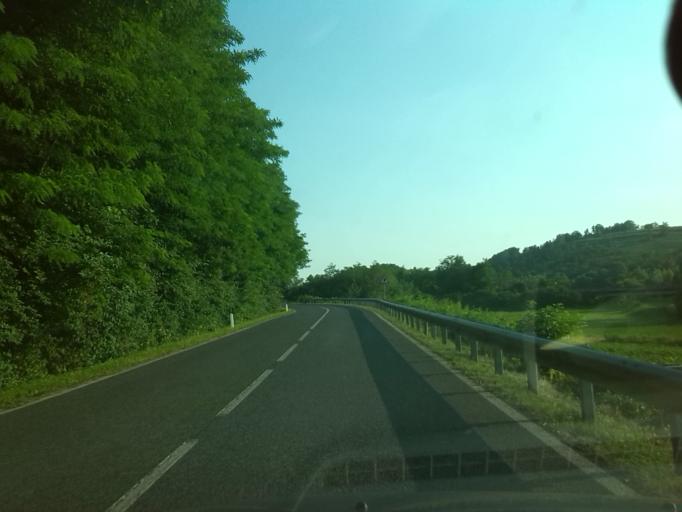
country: IT
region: Friuli Venezia Giulia
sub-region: Provincia di Gorizia
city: Dolegna del Collio
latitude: 46.0077
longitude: 13.4672
